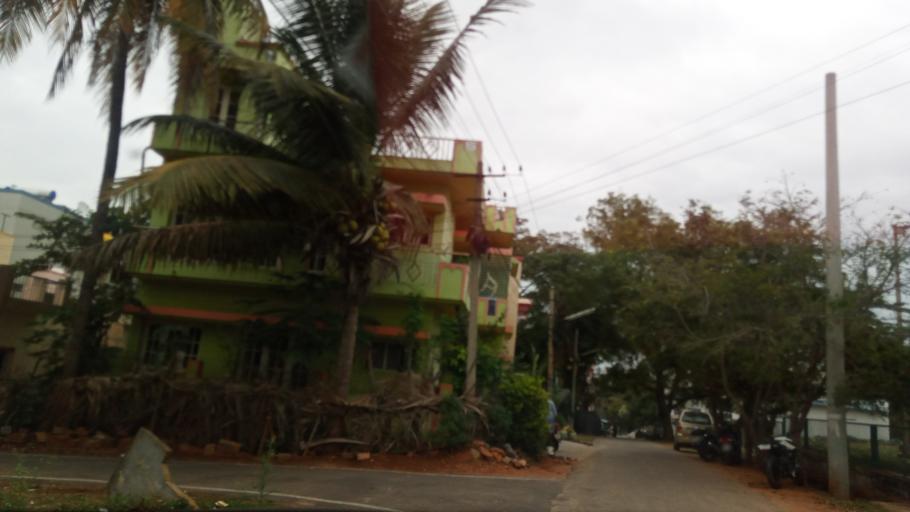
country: IN
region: Karnataka
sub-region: Mysore
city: Mysore
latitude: 12.2895
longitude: 76.6169
